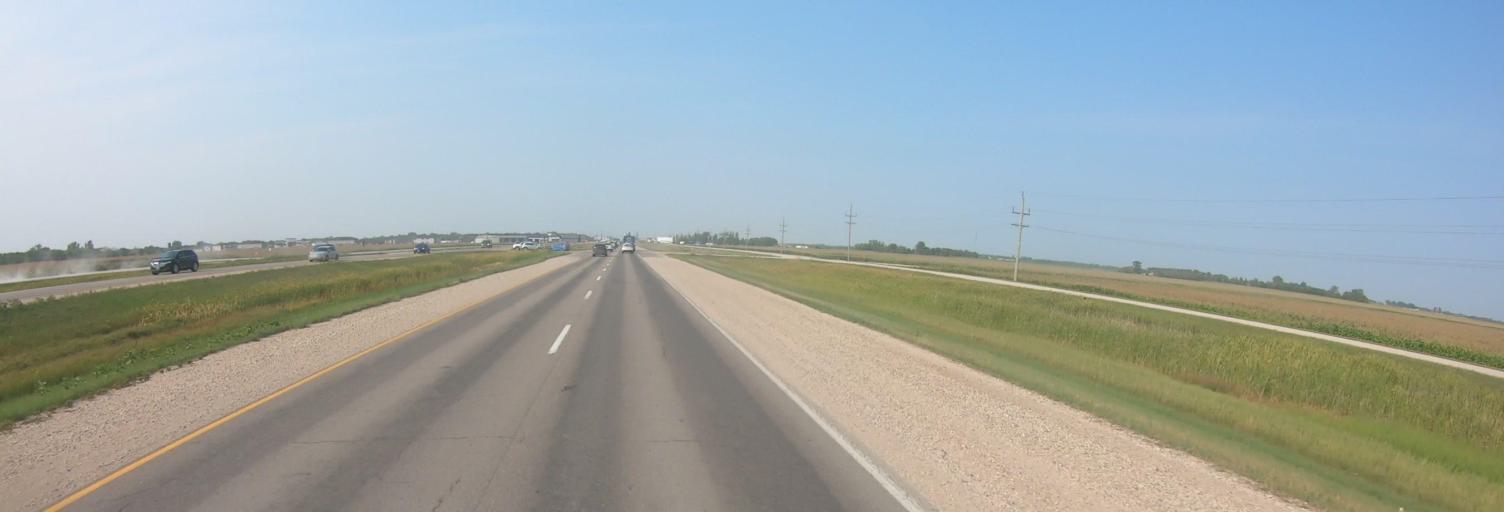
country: CA
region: Manitoba
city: Steinbach
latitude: 49.5881
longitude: -96.6875
